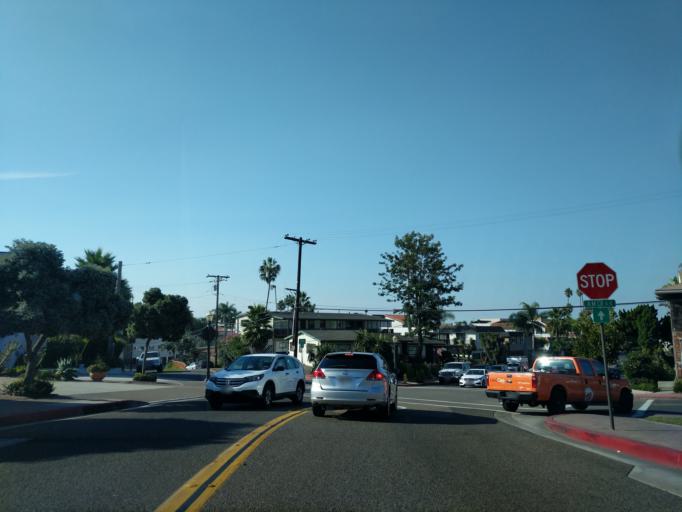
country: US
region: California
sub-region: Orange County
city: San Clemente
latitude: 33.4239
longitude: -117.6175
